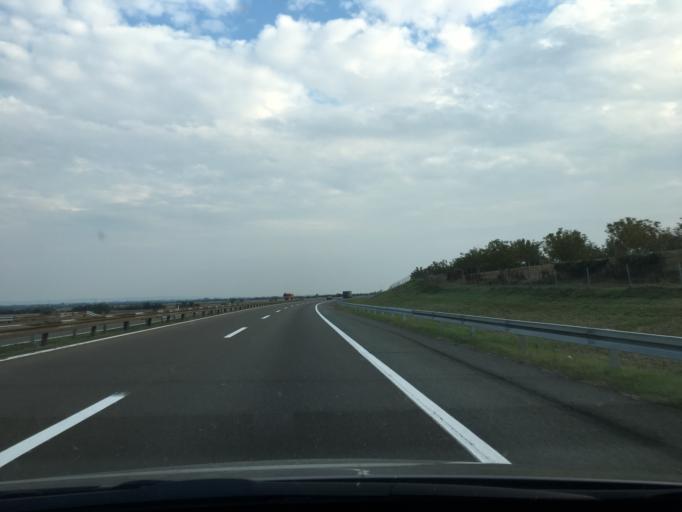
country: RS
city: Lugavcina
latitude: 44.4566
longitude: 21.0420
